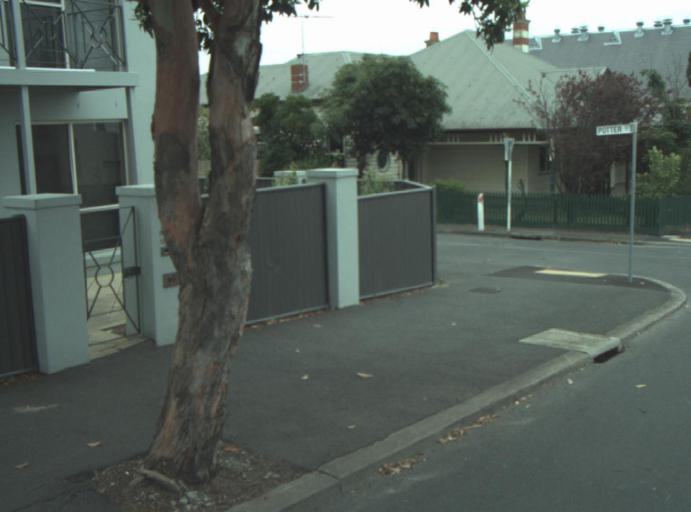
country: AU
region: Victoria
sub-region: Greater Geelong
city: Geelong West
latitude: -38.1464
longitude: 144.3472
